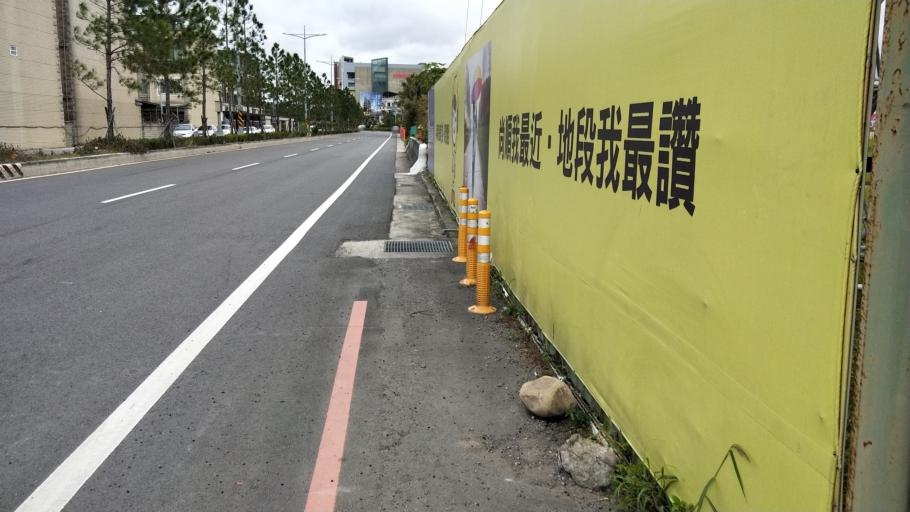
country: TW
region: Taiwan
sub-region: Hsinchu
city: Hsinchu
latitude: 24.6888
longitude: 120.8977
